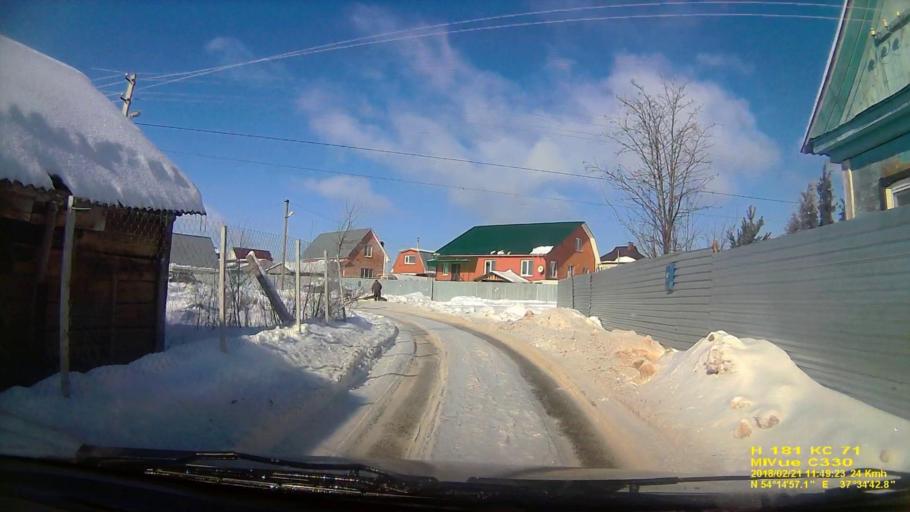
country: RU
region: Tula
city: Gorelki
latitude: 54.2496
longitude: 37.5795
